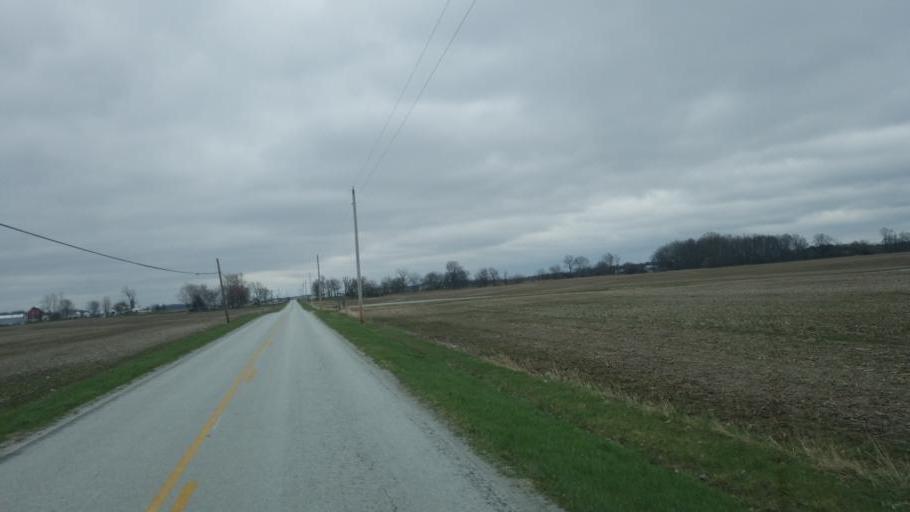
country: US
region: Ohio
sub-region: Hardin County
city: Kenton
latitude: 40.6584
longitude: -83.5472
